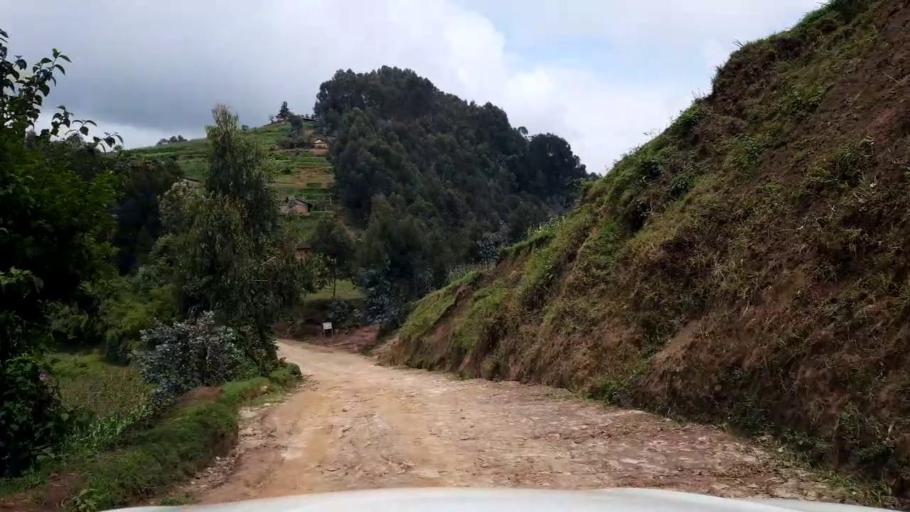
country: RW
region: Western Province
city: Kibuye
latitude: -1.9382
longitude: 29.4469
